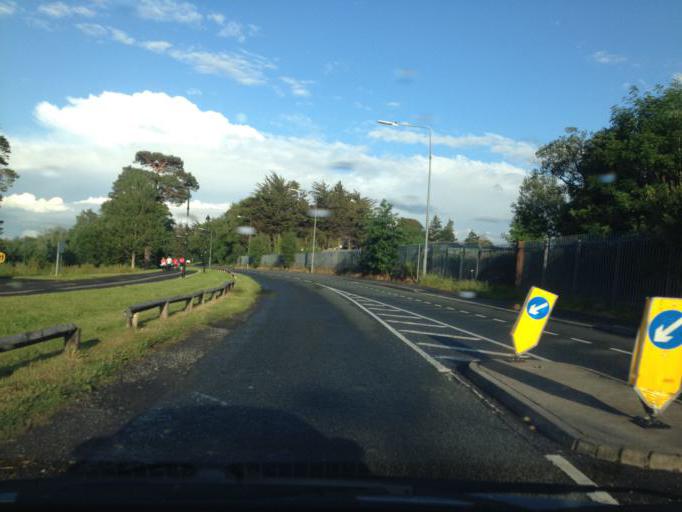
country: IE
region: Connaught
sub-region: Sligo
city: Sligo
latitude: 54.2659
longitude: -8.4530
